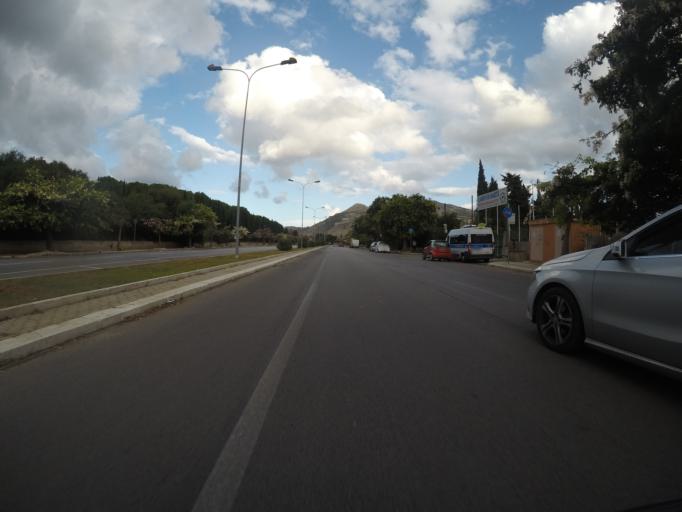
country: IT
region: Sicily
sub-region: Palermo
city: Palermo
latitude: 38.1889
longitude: 13.3112
